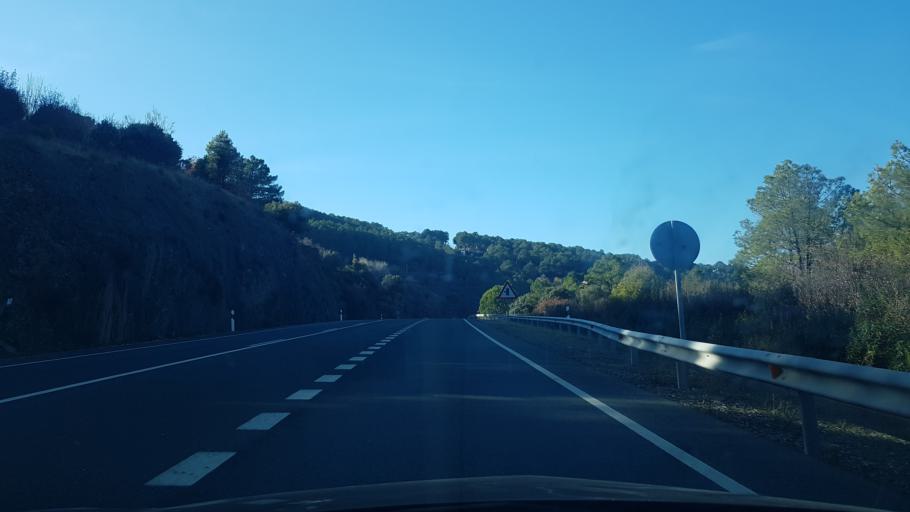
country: ES
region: Castille and Leon
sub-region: Provincia de Avila
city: El Tiemblo
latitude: 40.3853
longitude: -4.4569
